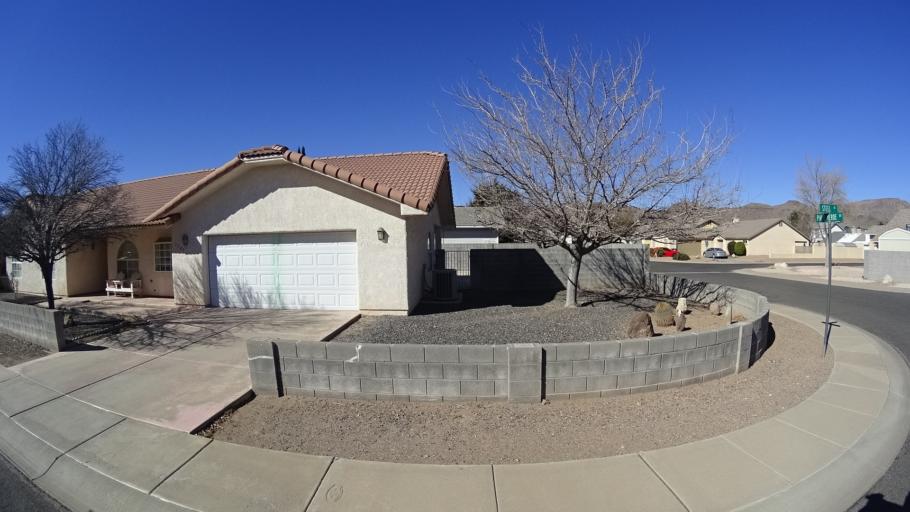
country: US
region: Arizona
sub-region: Mohave County
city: New Kingman-Butler
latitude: 35.2335
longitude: -114.0385
